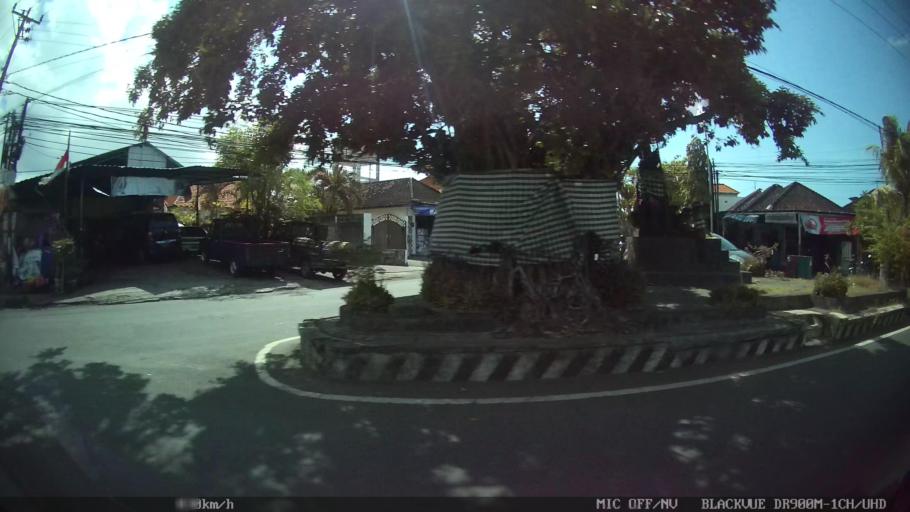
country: ID
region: Bali
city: Karyadharma
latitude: -8.7150
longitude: 115.2008
